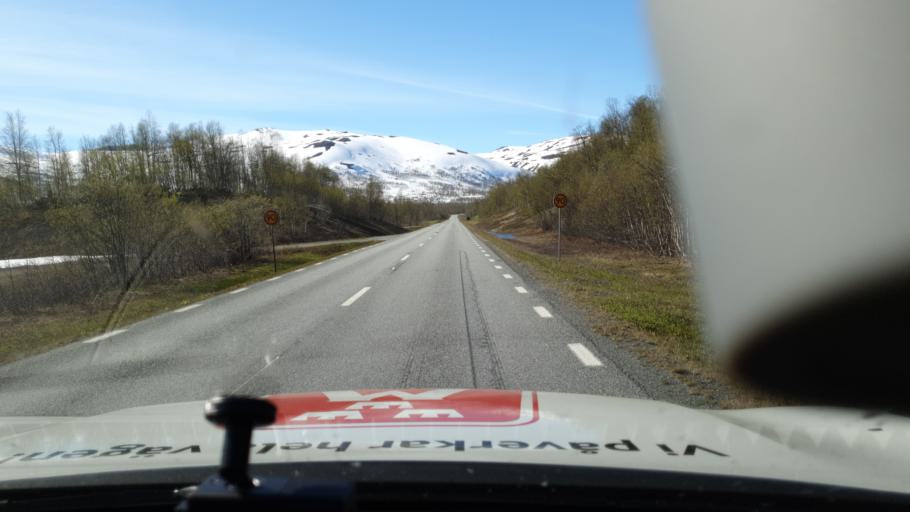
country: NO
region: Nordland
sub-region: Rana
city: Mo i Rana
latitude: 65.8761
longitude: 15.0042
